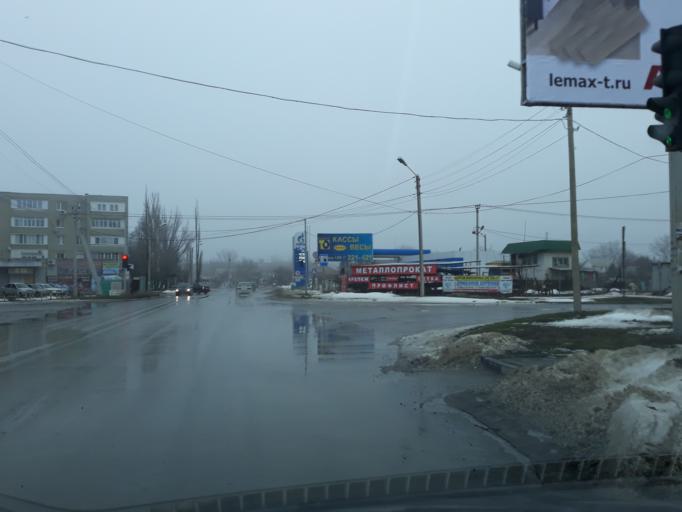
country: RU
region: Rostov
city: Taganrog
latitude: 47.2151
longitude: 38.8787
